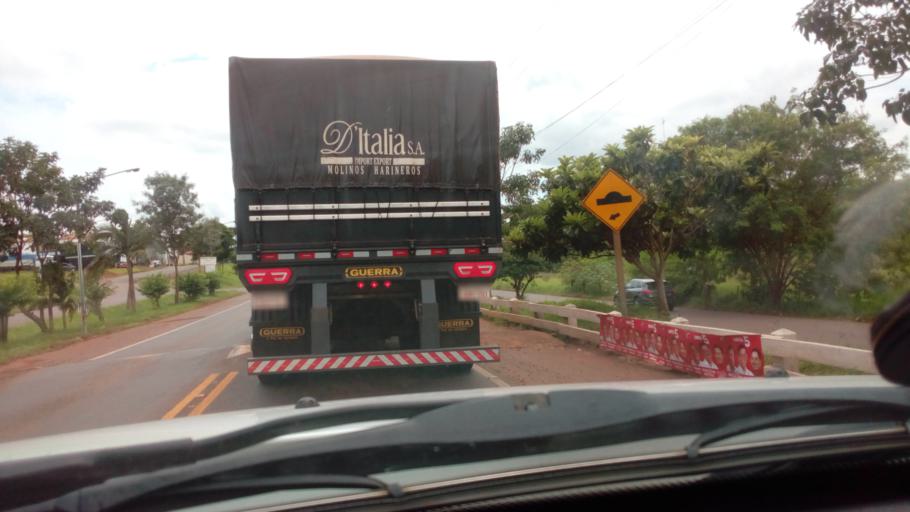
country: PY
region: Alto Parana
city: Santa Rita
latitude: -25.7906
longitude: -55.0846
